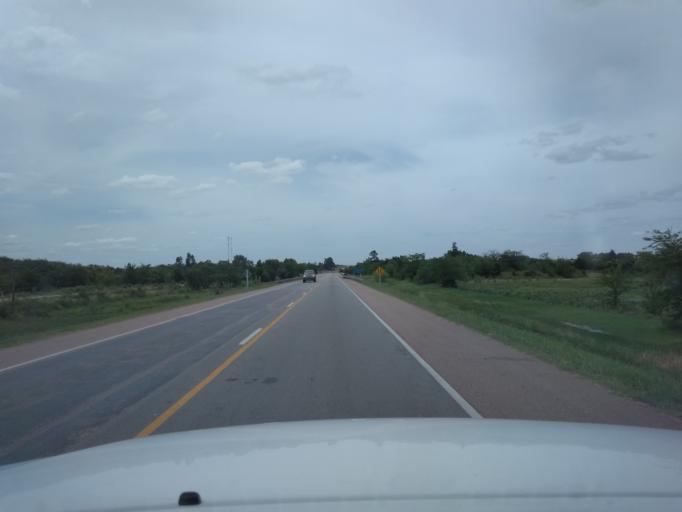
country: UY
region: Canelones
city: Canelones
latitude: -34.5042
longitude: -56.2815
